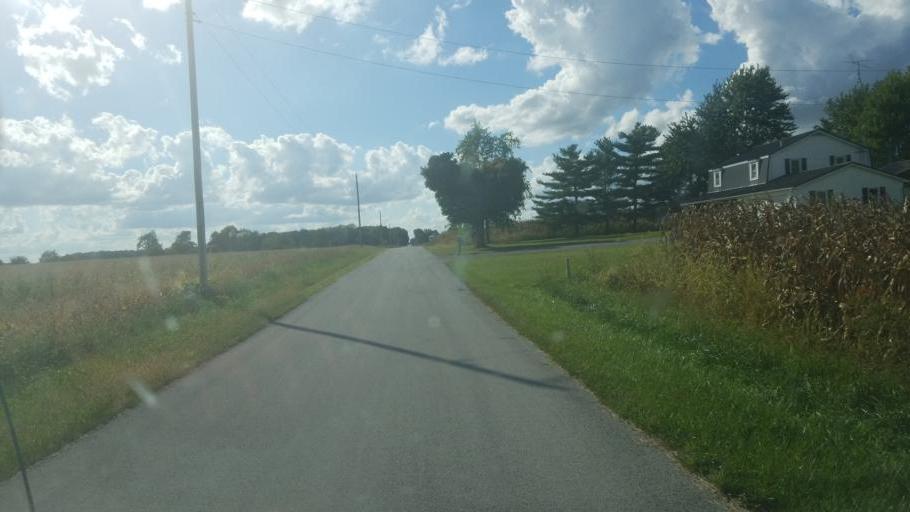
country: US
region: Ohio
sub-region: Hardin County
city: Kenton
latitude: 40.7181
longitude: -83.6936
